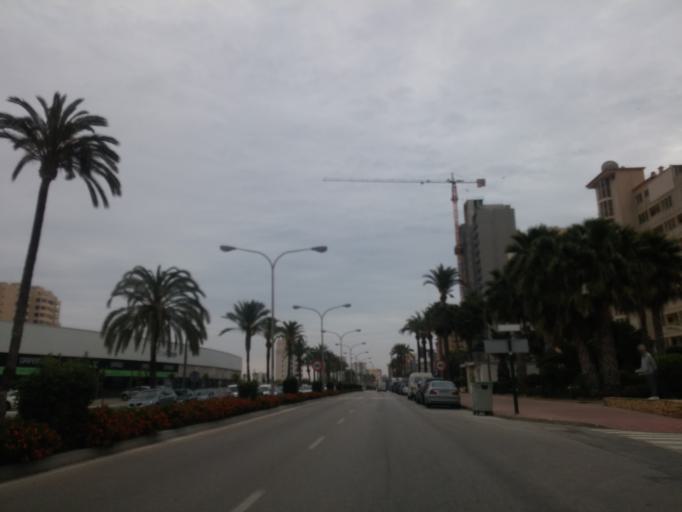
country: ES
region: Valencia
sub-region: Provincia de Alicante
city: Calp
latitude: 38.6442
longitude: 0.0547
